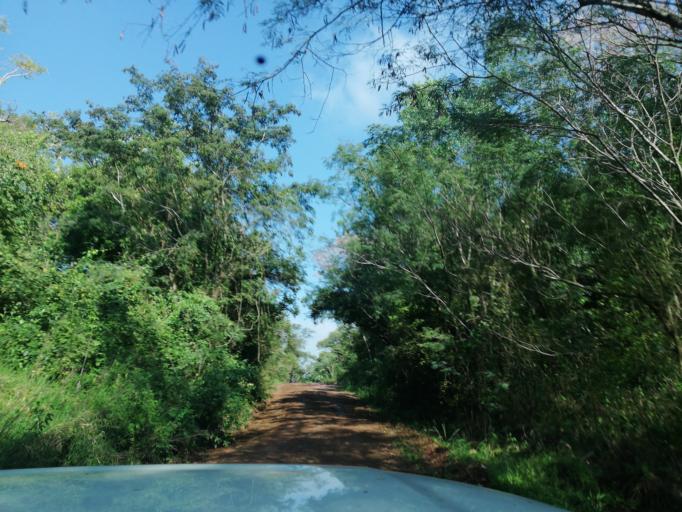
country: AR
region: Misiones
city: Cerro Azul
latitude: -27.6194
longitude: -55.5252
